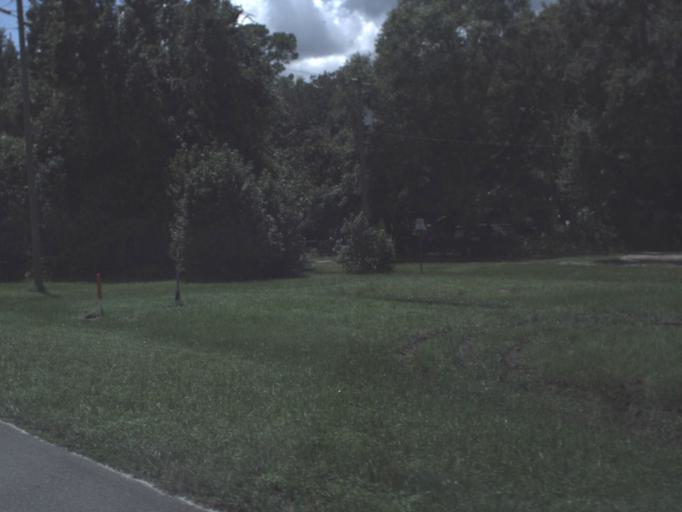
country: US
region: Florida
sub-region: Pasco County
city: Crystal Springs
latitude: 28.1843
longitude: -82.1585
